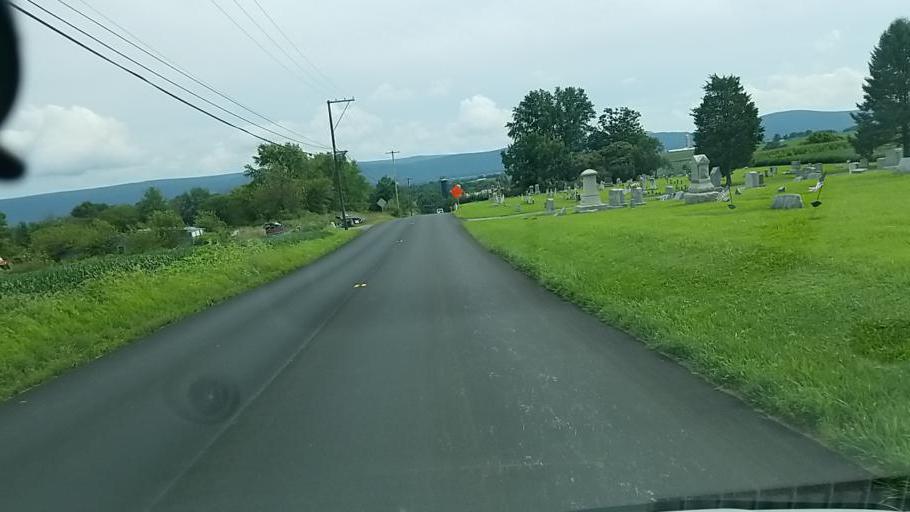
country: US
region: Pennsylvania
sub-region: Dauphin County
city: Elizabethville
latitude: 40.5988
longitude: -76.8107
